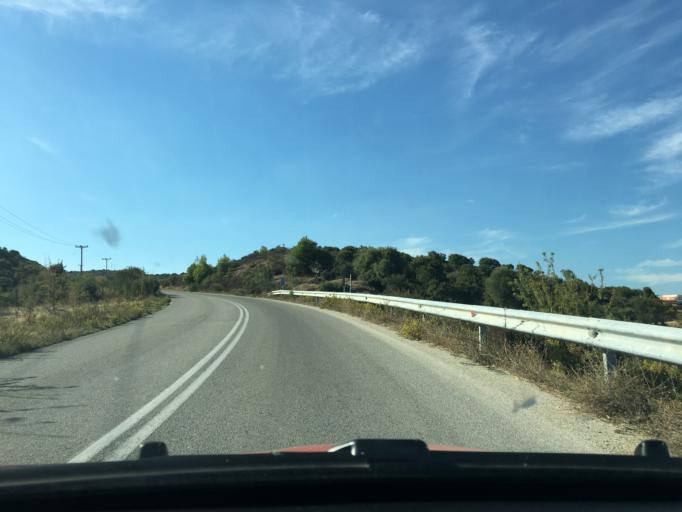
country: GR
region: Central Macedonia
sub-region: Nomos Chalkidikis
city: Ierissos
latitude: 40.3789
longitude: 23.8466
